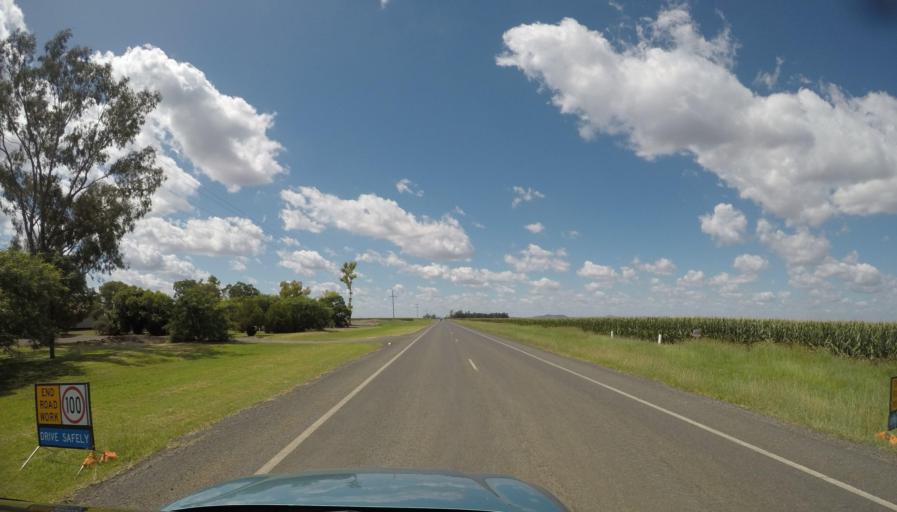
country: AU
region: Queensland
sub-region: Toowoomba
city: Oakey
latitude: -27.5188
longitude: 151.4196
